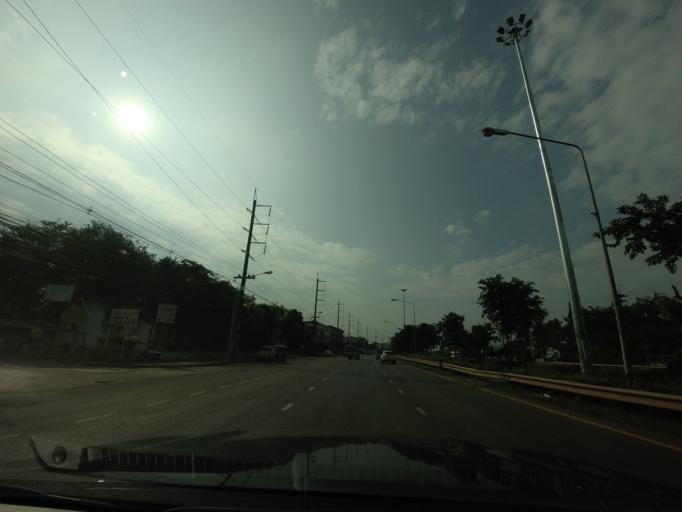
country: TH
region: Nong Khai
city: Nong Khai
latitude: 17.8644
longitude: 102.7483
